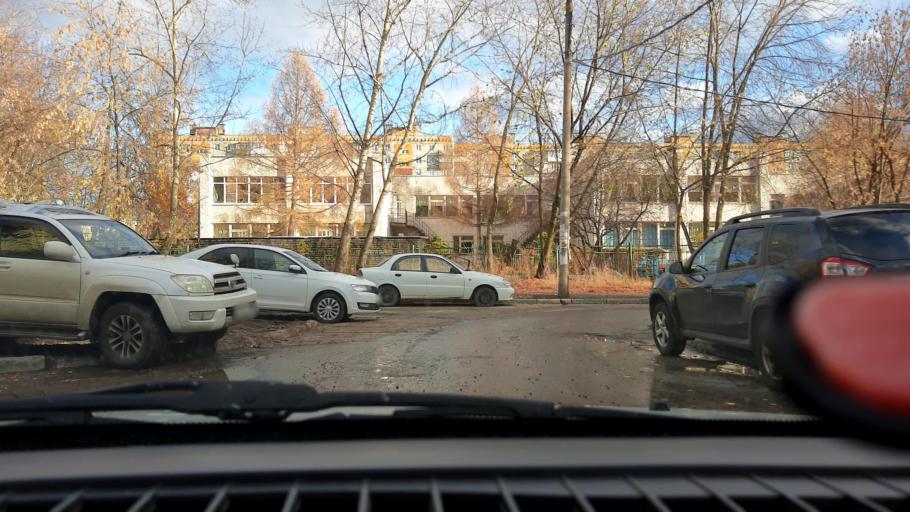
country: RU
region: Nizjnij Novgorod
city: Nizhniy Novgorod
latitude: 56.2768
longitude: 43.9476
